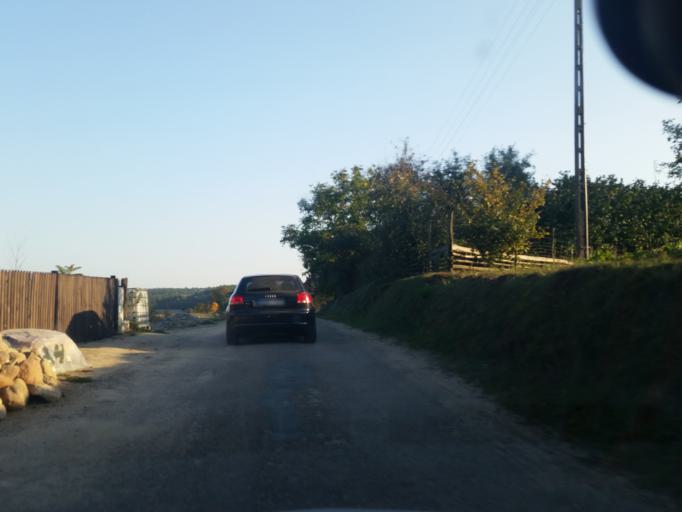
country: PL
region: Kujawsko-Pomorskie
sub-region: Powiat brodnicki
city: Bartniczka
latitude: 53.2834
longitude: 19.6976
